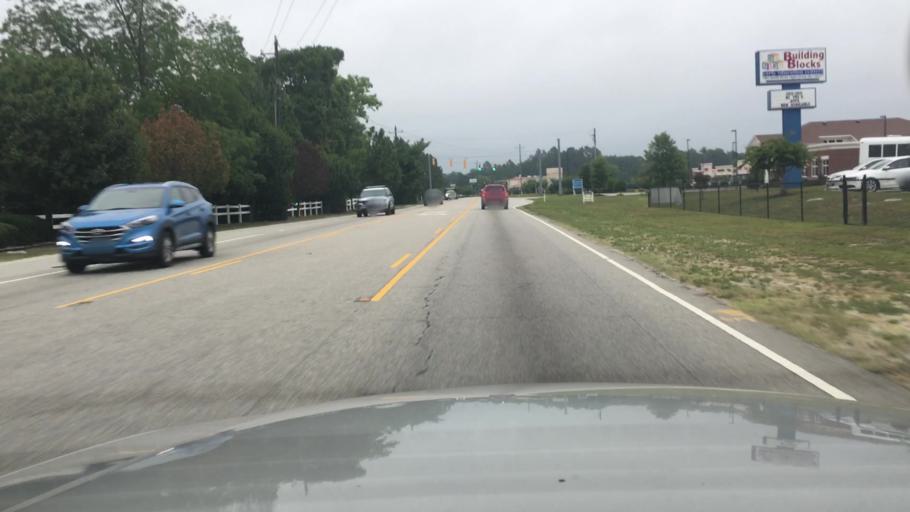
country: US
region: North Carolina
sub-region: Cumberland County
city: Hope Mills
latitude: 34.9801
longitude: -78.9778
